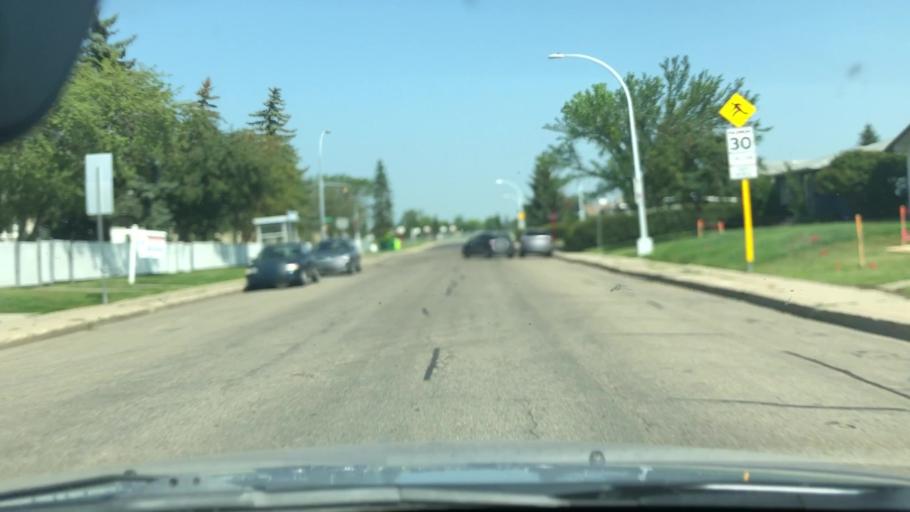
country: CA
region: Alberta
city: Edmonton
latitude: 53.6057
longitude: -113.4734
